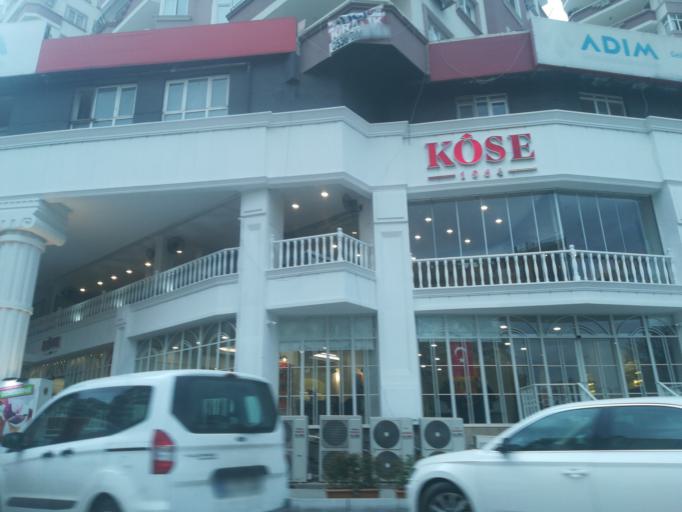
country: TR
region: Adana
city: Adana
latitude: 37.0360
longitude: 35.2942
